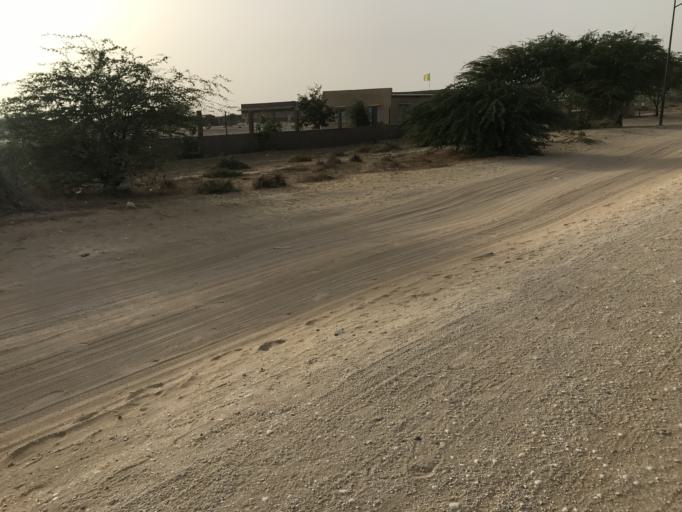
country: SN
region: Saint-Louis
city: Saint-Louis
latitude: 16.0250
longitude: -16.4459
